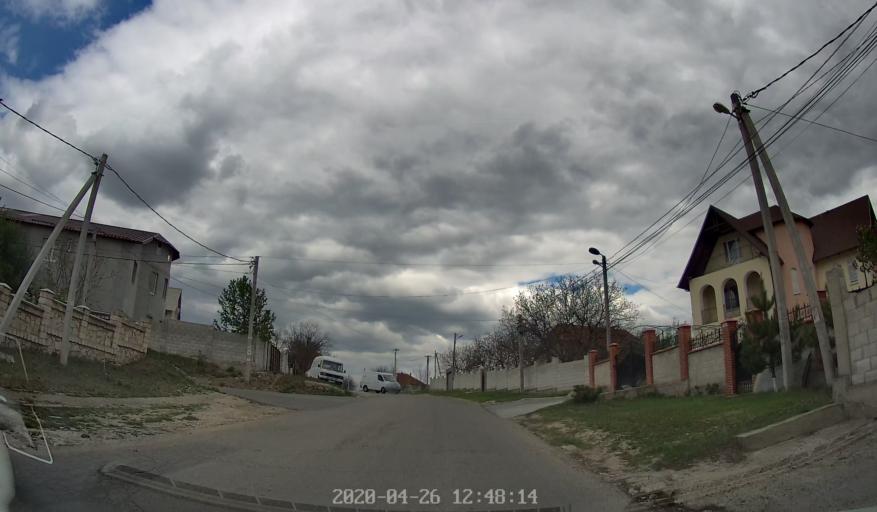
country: MD
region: Chisinau
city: Vadul lui Voda
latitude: 47.0677
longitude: 29.0148
